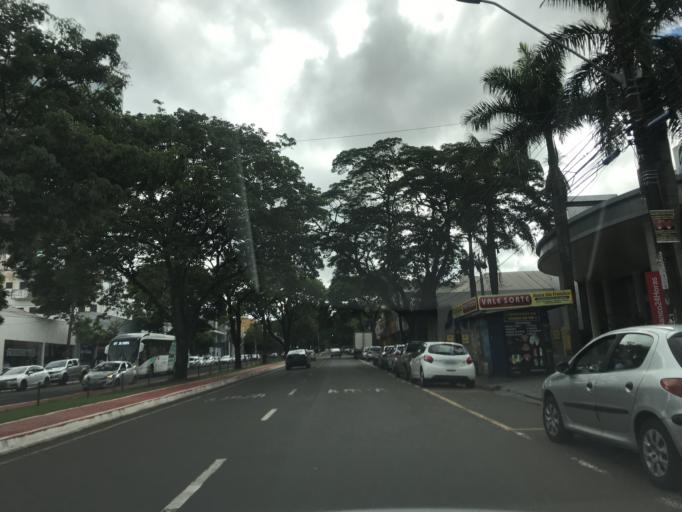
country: BR
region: Parana
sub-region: Maringa
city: Maringa
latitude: -23.4210
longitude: -51.9477
